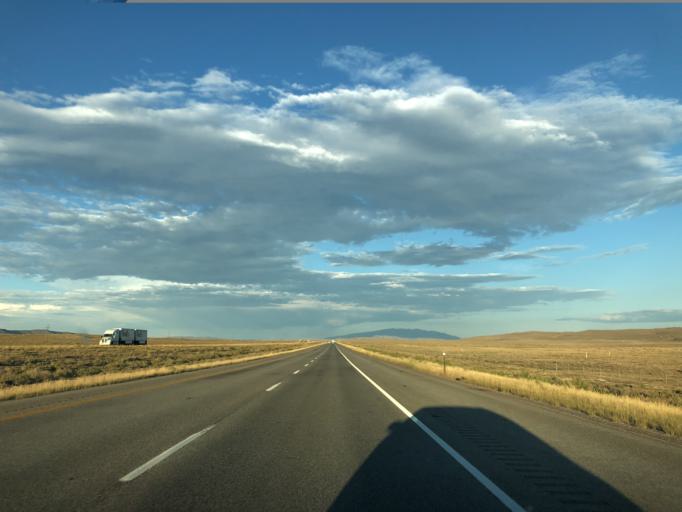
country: US
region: Wyoming
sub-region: Carbon County
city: Rawlins
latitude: 41.7680
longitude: -107.0415
